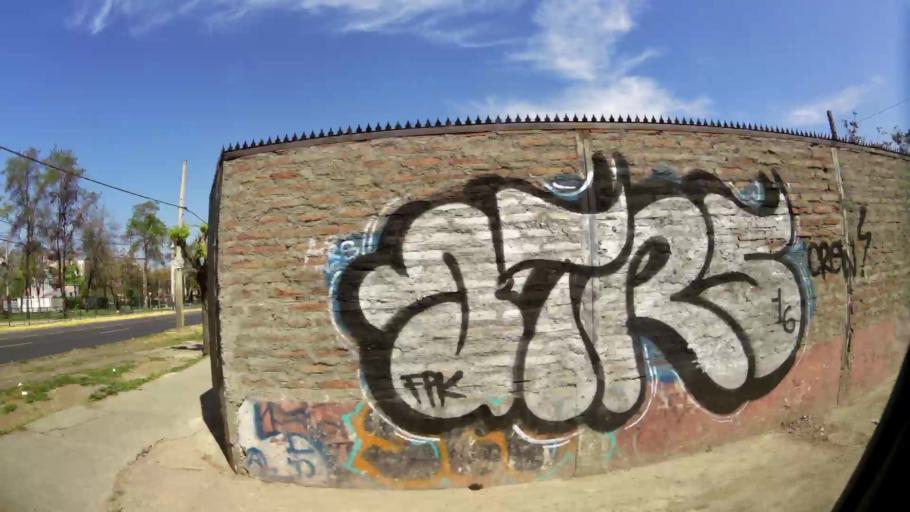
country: CL
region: Santiago Metropolitan
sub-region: Provincia de Santiago
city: Lo Prado
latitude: -33.4712
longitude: -70.7194
